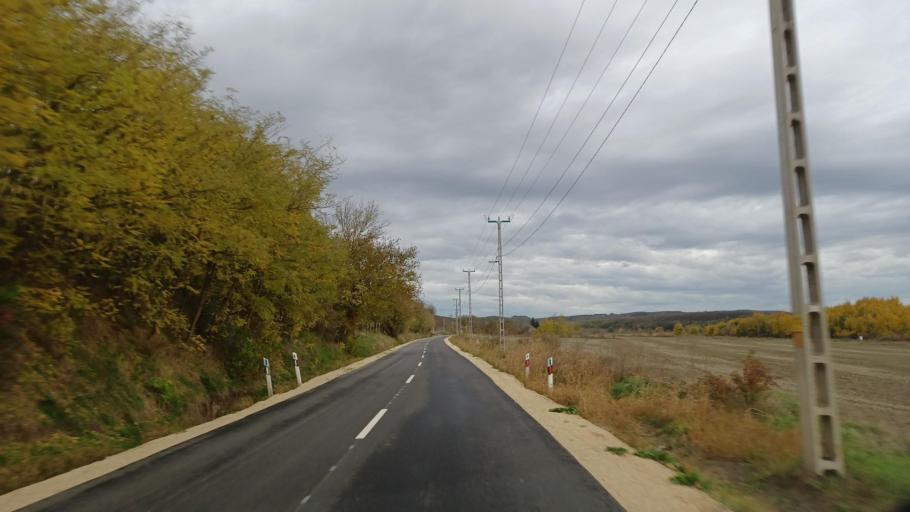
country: HU
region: Tolna
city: Gyonk
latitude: 46.6056
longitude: 18.4234
